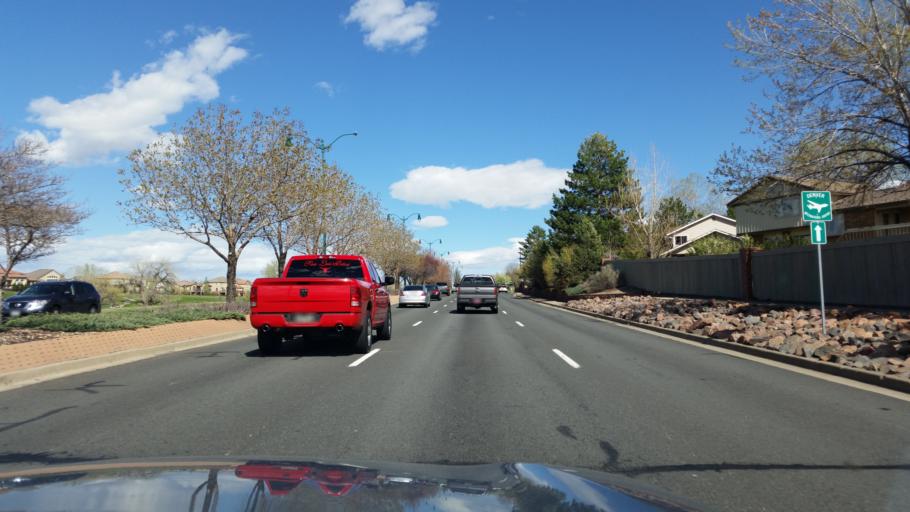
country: US
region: Colorado
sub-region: Broomfield County
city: Broomfield
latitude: 39.8852
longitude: -105.0512
